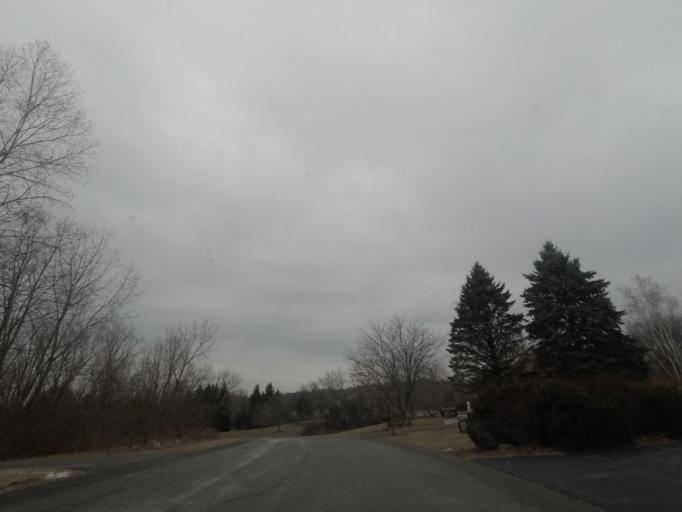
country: US
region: New York
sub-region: Rensselaer County
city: East Greenbush
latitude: 42.5629
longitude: -73.6484
